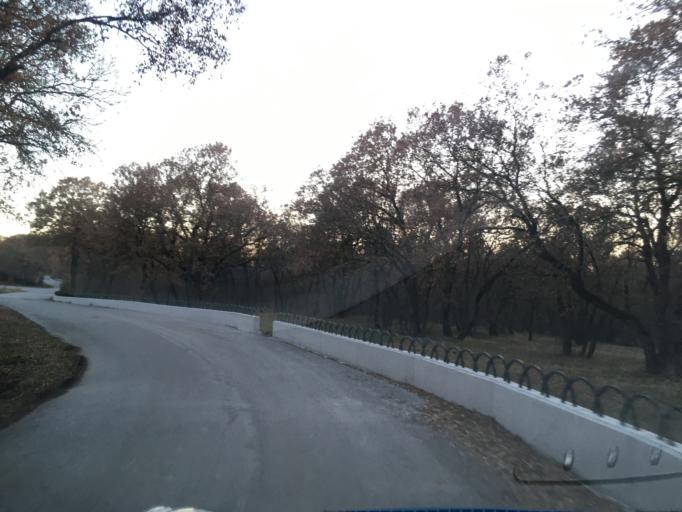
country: GR
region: West Macedonia
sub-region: Nomos Kozanis
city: Koila
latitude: 40.3296
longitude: 21.8319
